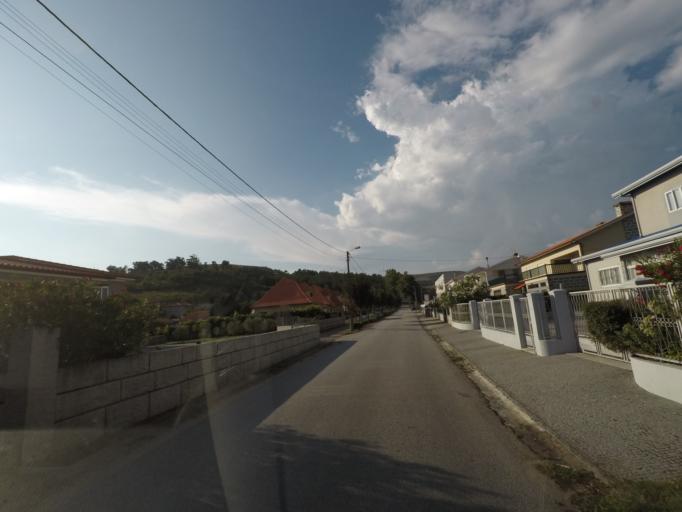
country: PT
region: Porto
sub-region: Baiao
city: Valadares
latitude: 41.1669
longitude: -7.9372
